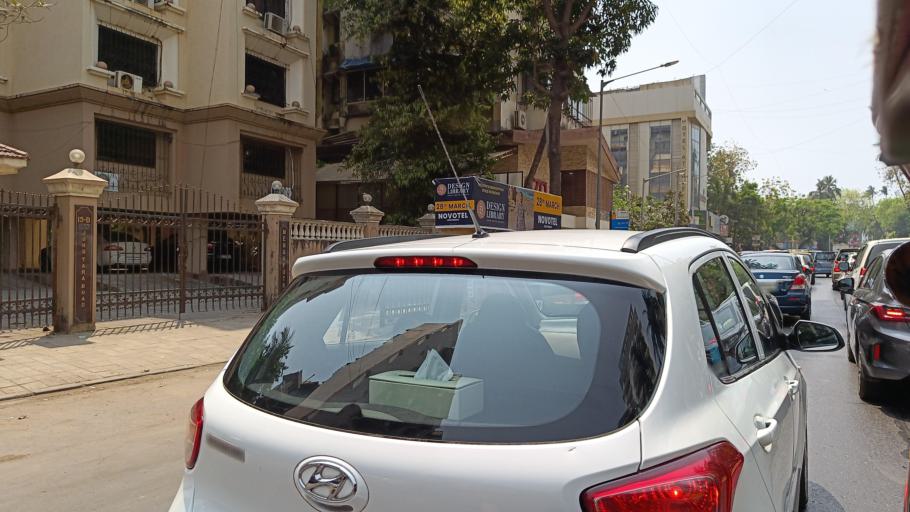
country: IN
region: Maharashtra
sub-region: Mumbai Suburban
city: Mumbai
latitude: 19.0905
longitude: 72.8276
